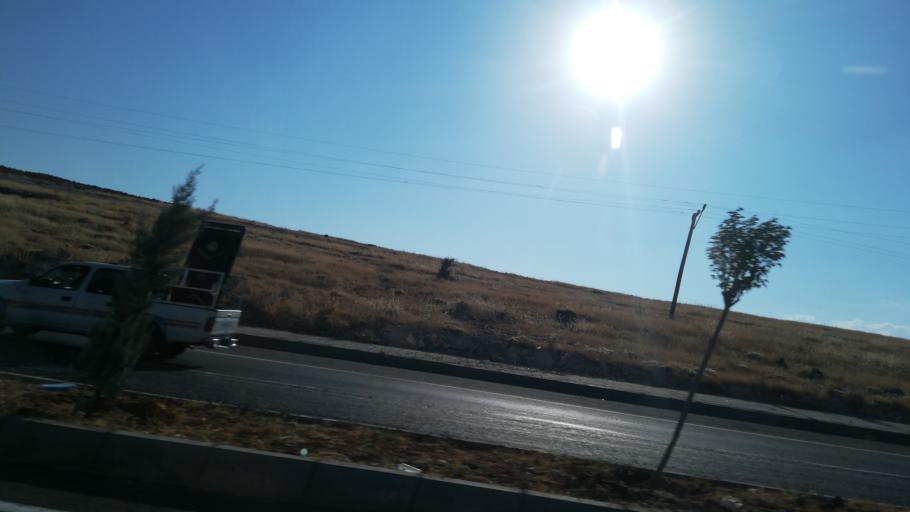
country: TR
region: Mardin
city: Midyat
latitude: 37.4001
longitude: 41.3440
